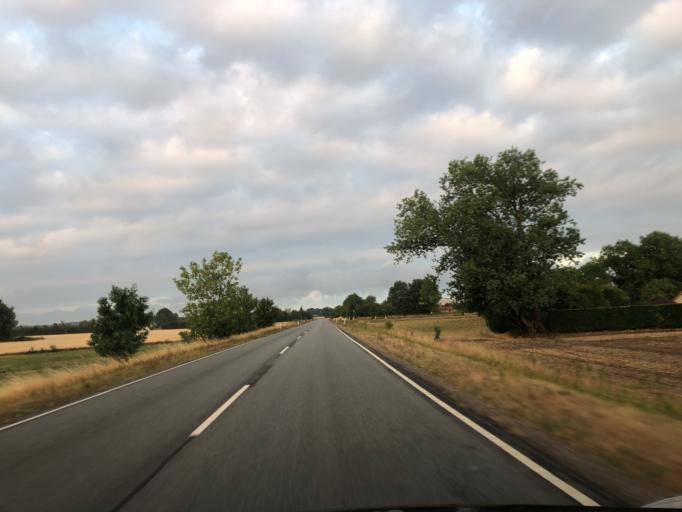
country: DK
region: Zealand
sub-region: Slagelse Kommune
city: Slagelse
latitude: 55.4452
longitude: 11.4267
